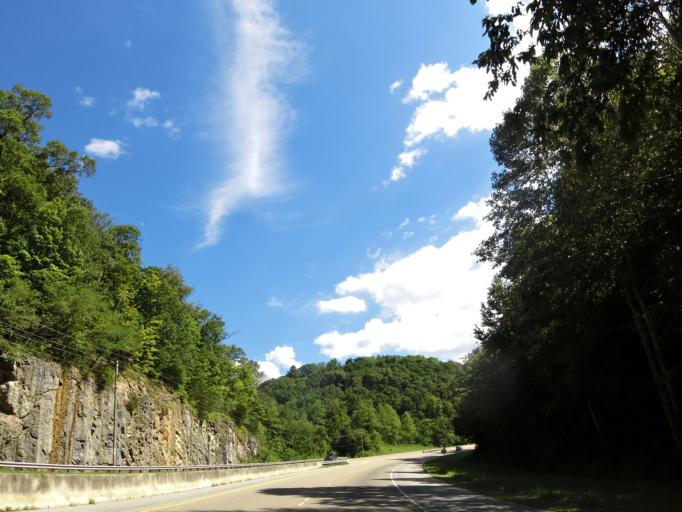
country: US
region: Tennessee
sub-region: Grainger County
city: Rutledge
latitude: 36.3643
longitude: -83.4329
